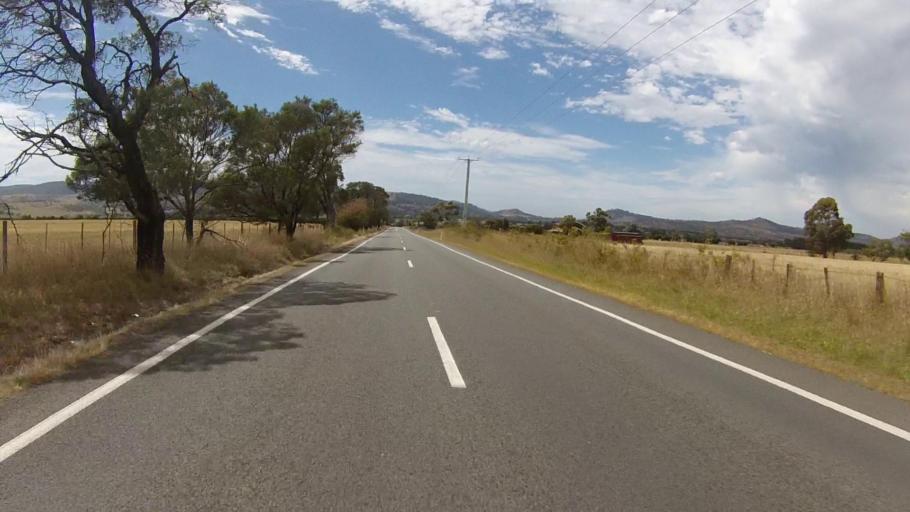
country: AU
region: Tasmania
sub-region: Clarence
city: Cambridge
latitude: -42.6789
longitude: 147.4248
